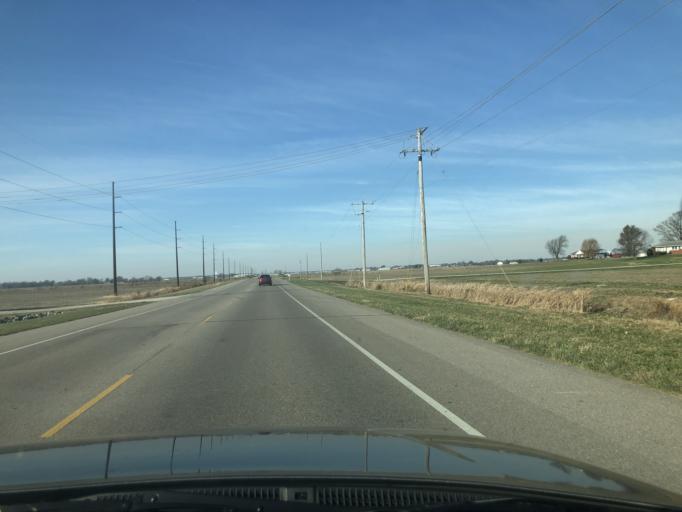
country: US
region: Indiana
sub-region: Warrick County
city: Newburgh
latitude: 37.9913
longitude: -87.4186
